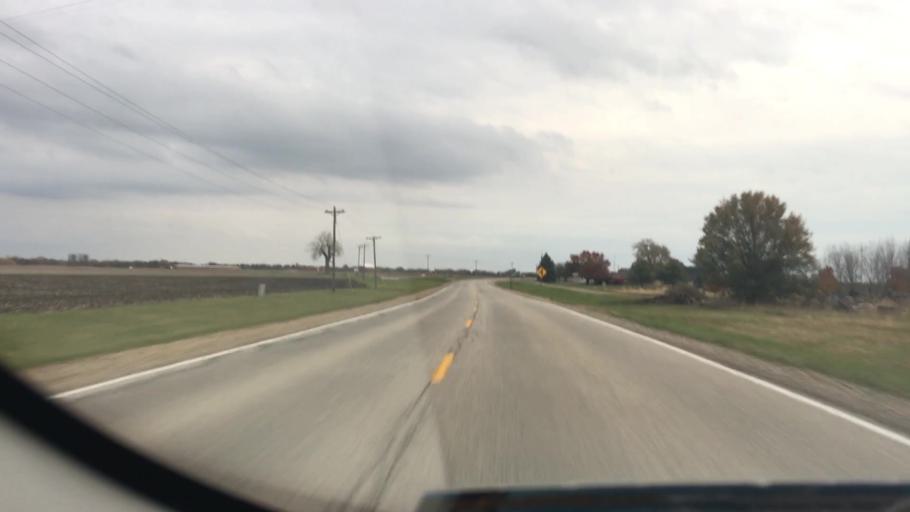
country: US
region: Illinois
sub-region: McLean County
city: Twin Grove
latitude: 40.5177
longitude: -89.0444
